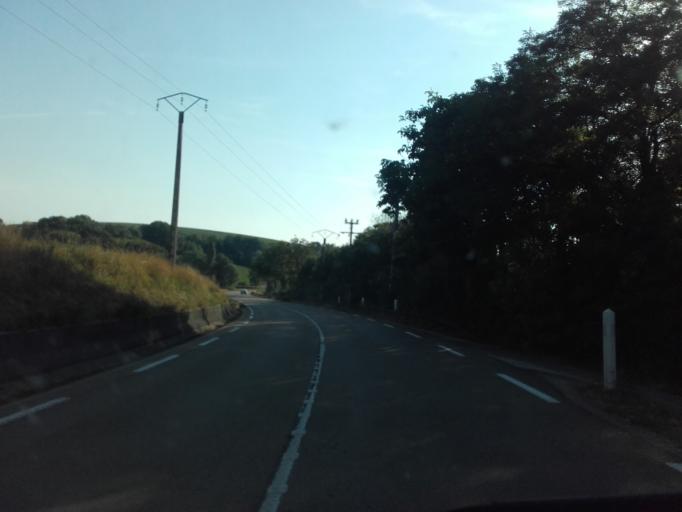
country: FR
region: Bourgogne
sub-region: Departement de l'Yonne
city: Chablis
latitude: 47.8203
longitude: 3.7383
